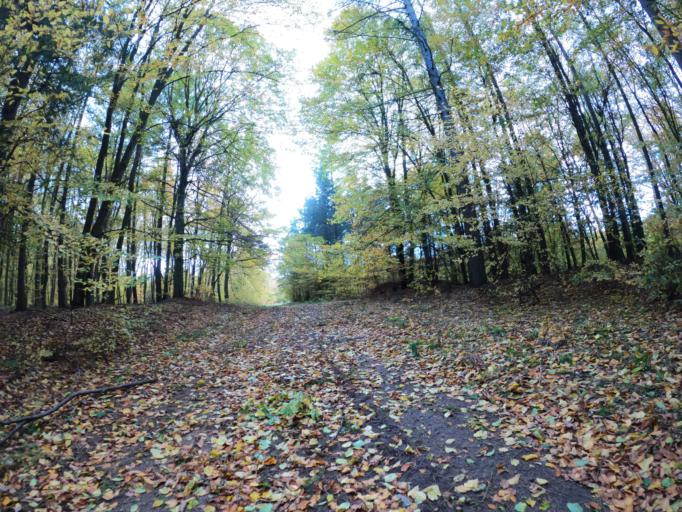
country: PL
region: West Pomeranian Voivodeship
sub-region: Powiat mysliborski
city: Barlinek
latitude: 52.9627
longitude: 15.2631
